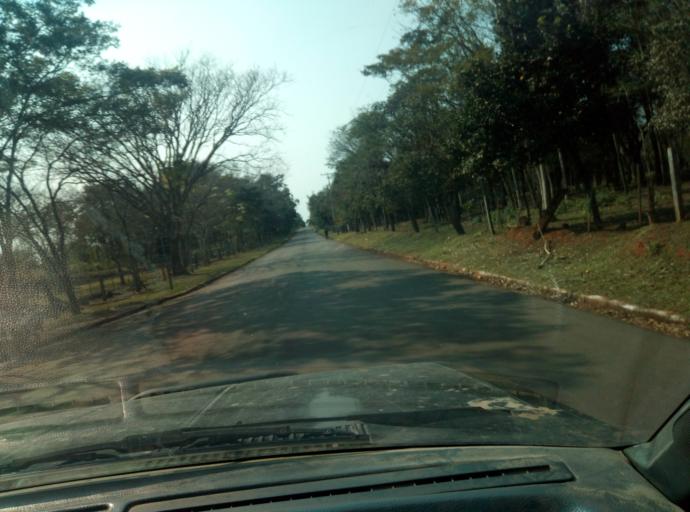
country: PY
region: Caaguazu
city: Carayao
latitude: -25.2105
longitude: -56.2973
